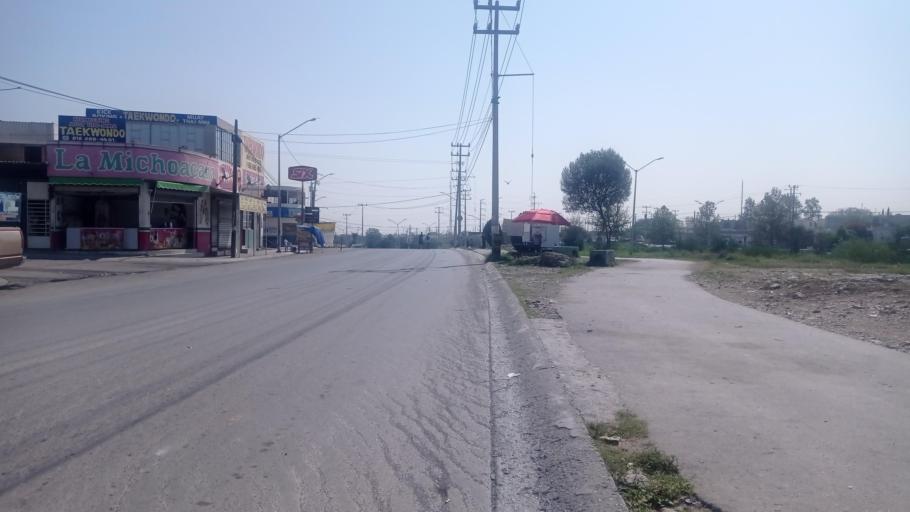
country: MX
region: Nuevo Leon
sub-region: Juarez
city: Monte Kristal
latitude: 25.6101
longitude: -100.1603
